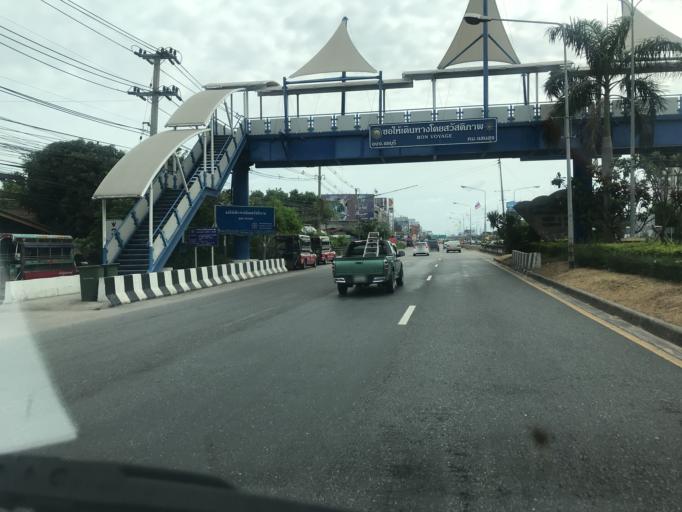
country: TH
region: Chon Buri
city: Chon Buri
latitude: 13.2878
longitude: 100.9399
